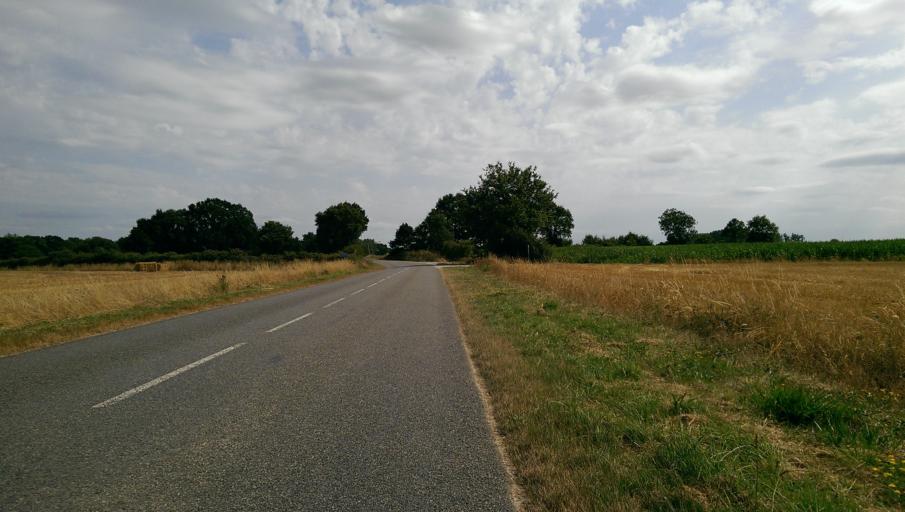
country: FR
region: Pays de la Loire
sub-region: Departement de la Loire-Atlantique
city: La Planche
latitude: 46.9988
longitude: -1.4297
